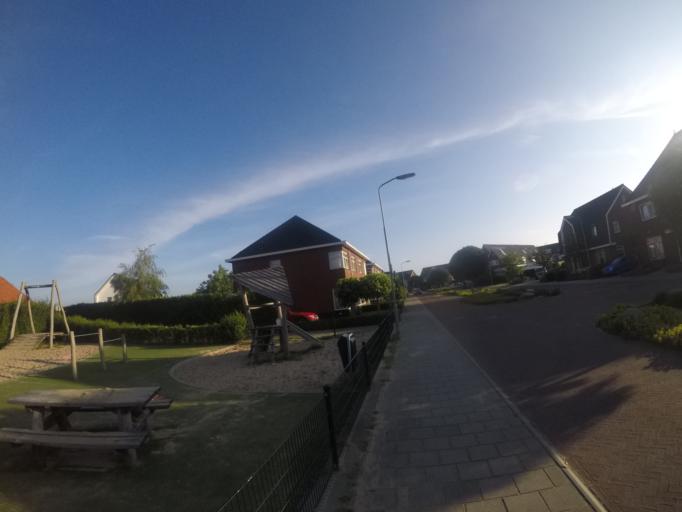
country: NL
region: Gelderland
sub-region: Gemeente Westervoort
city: Westervoort
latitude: 51.9596
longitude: 5.9612
